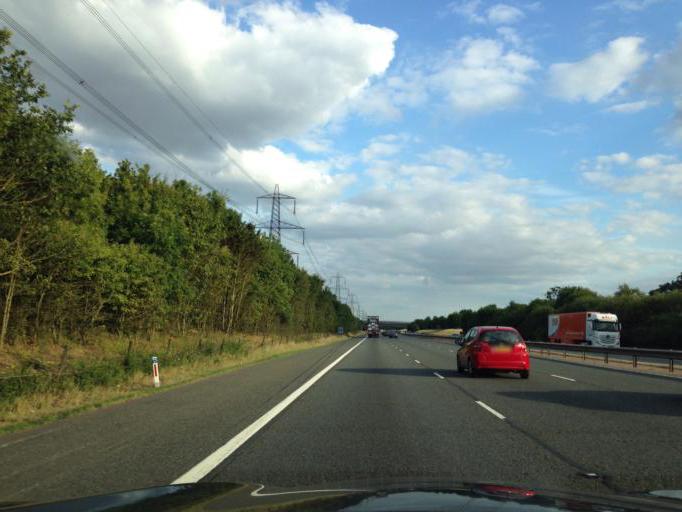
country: GB
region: England
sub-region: Oxfordshire
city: Wheatley
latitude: 51.8033
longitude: -1.0940
